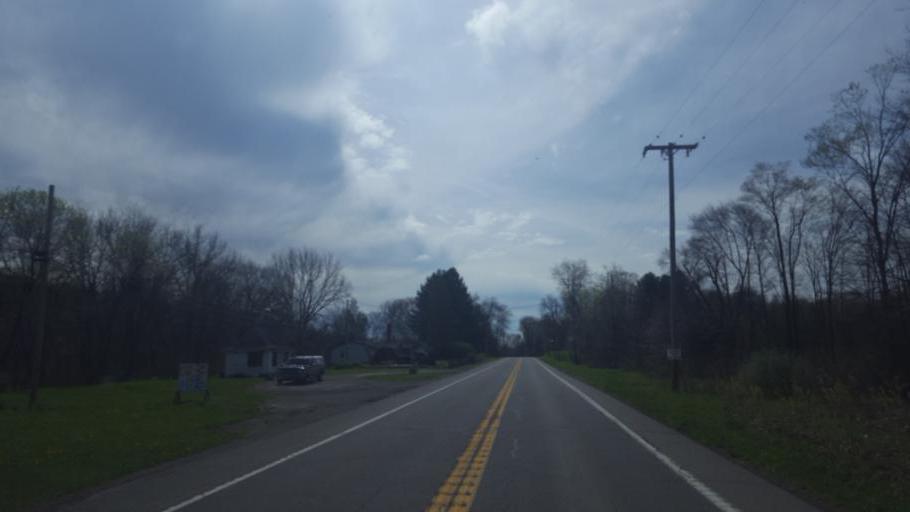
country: US
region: Pennsylvania
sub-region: Mercer County
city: Stoneboro
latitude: 41.3526
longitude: -80.0700
